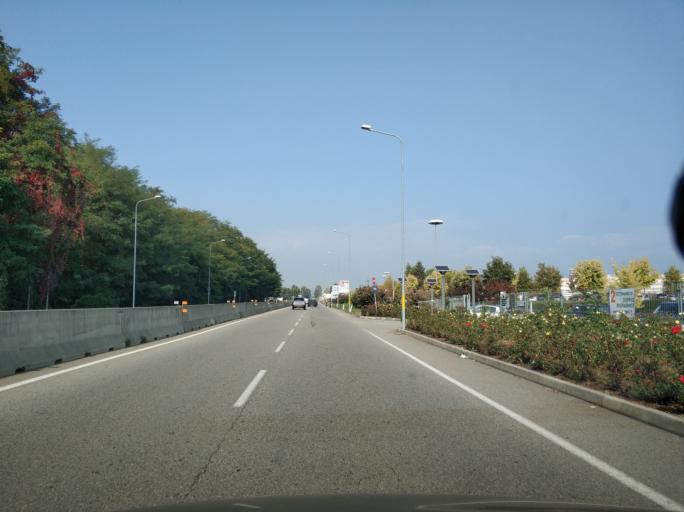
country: IT
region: Piedmont
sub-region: Provincia di Biella
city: Gaglianico
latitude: 45.5454
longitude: 8.0758
